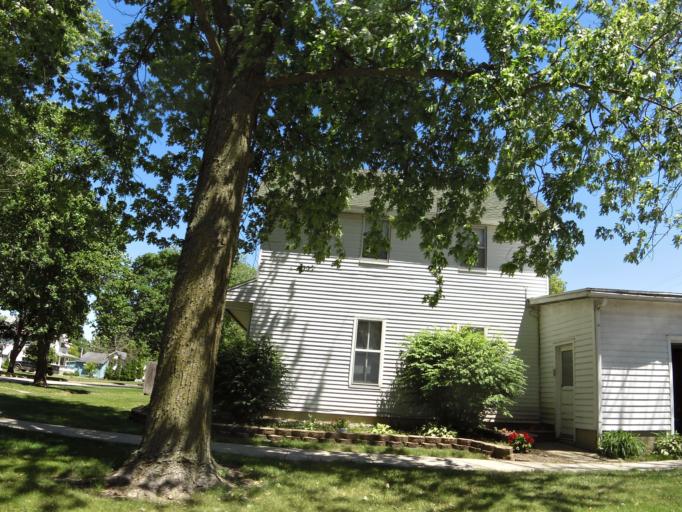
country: US
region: Illinois
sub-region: Livingston County
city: Forrest
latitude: 40.7502
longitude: -88.4092
